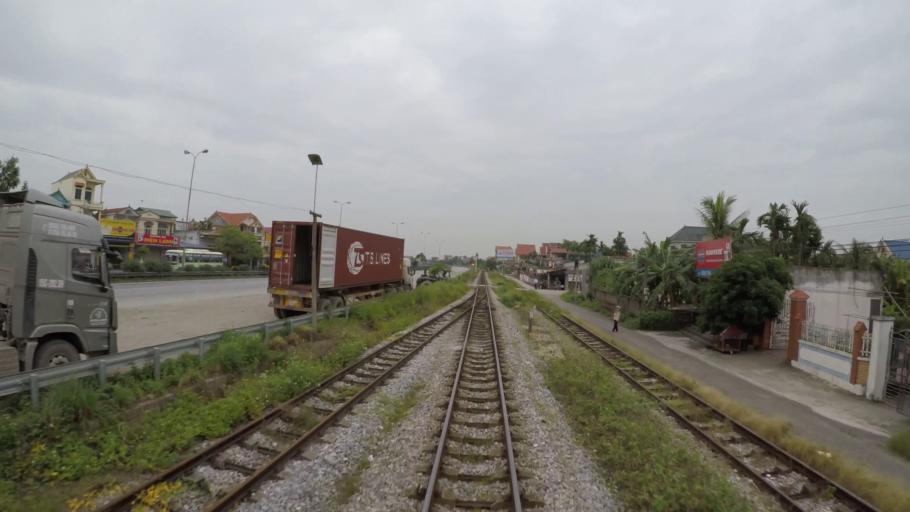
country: VN
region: Hai Duong
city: Phu Thai
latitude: 20.9728
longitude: 106.4395
